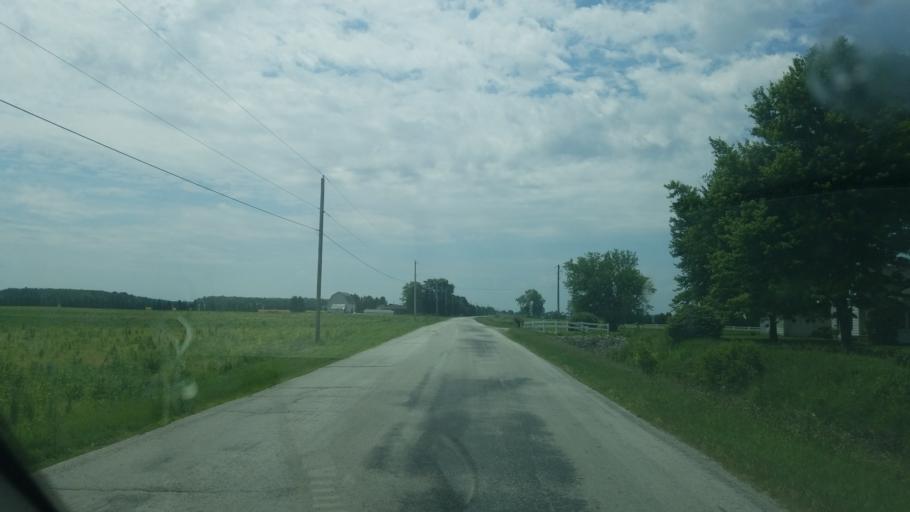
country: US
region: Ohio
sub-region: Wood County
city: Bowling Green
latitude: 41.2923
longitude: -83.5927
